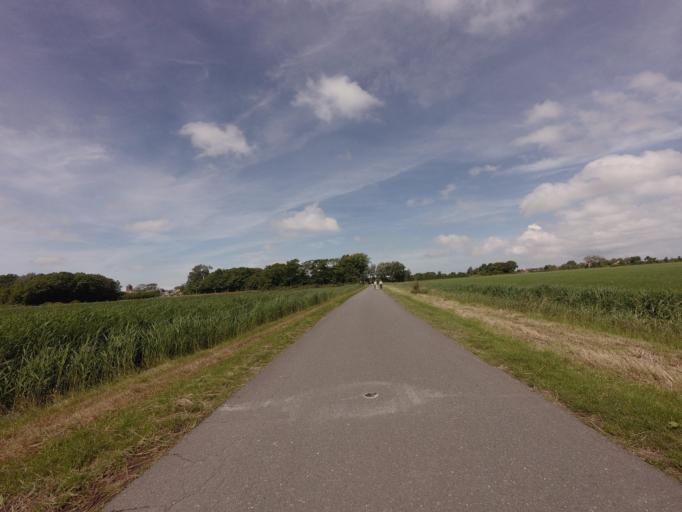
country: NL
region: North Holland
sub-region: Gemeente Texel
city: Den Burg
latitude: 53.0816
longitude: 4.8804
